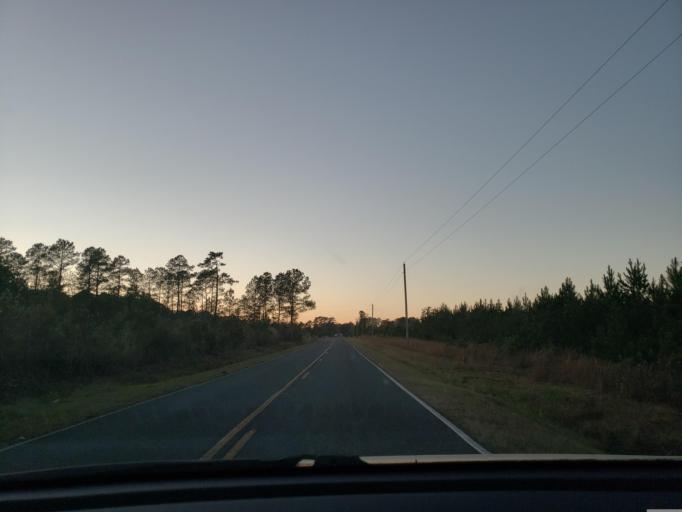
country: US
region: North Carolina
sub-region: Onslow County
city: Richlands
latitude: 34.7385
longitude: -77.6278
